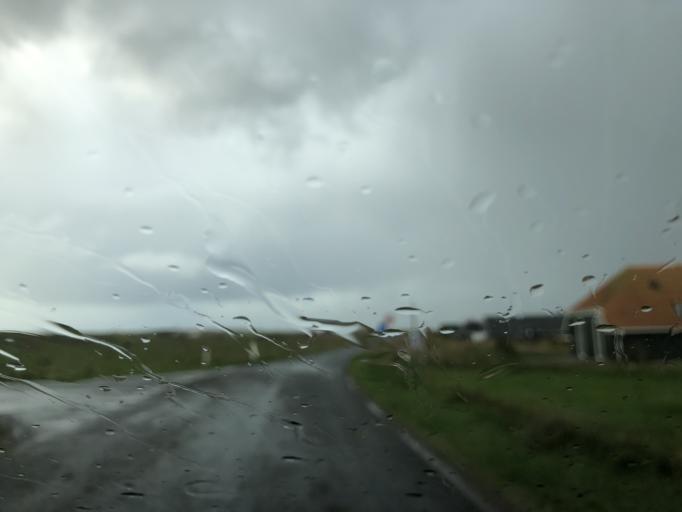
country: DK
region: Central Jutland
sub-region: Lemvig Kommune
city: Harboore
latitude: 56.5383
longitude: 8.1322
